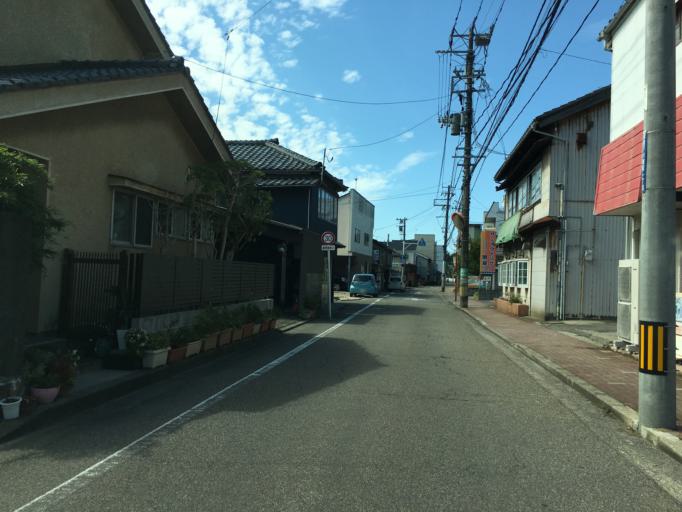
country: JP
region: Niigata
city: Niigata-shi
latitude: 37.9161
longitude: 139.0270
